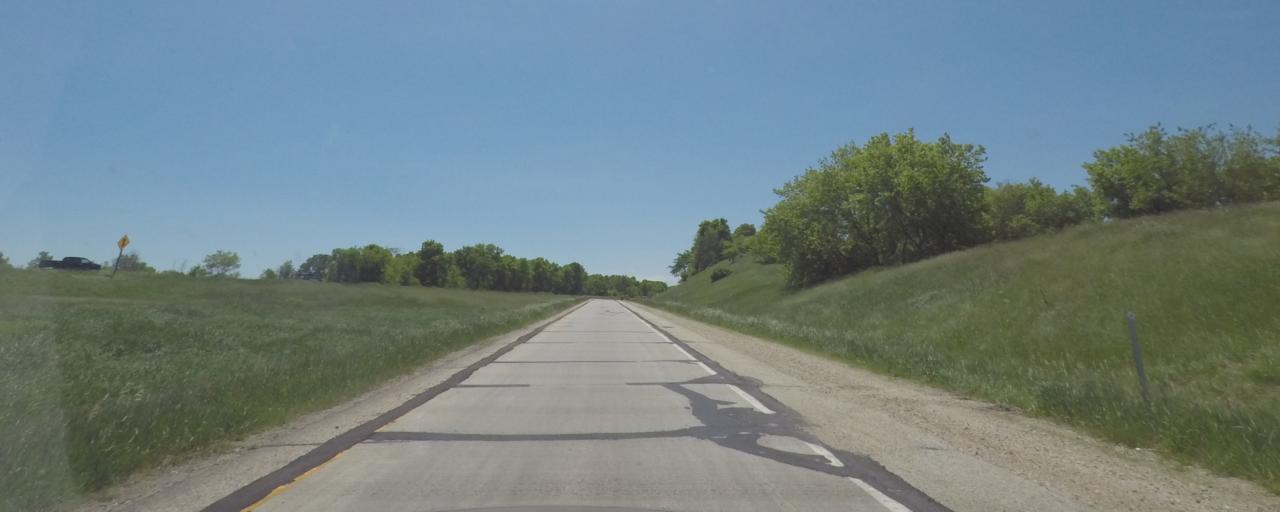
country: US
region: Wisconsin
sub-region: Washington County
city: West Bend
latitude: 43.4544
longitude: -88.2070
